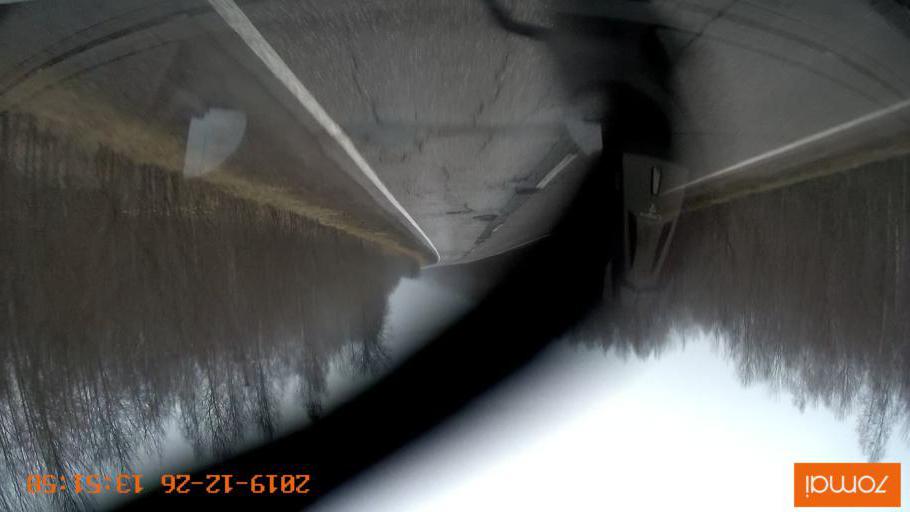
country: RU
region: Jaroslavl
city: Poshekhon'ye
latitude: 58.6378
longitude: 38.5971
